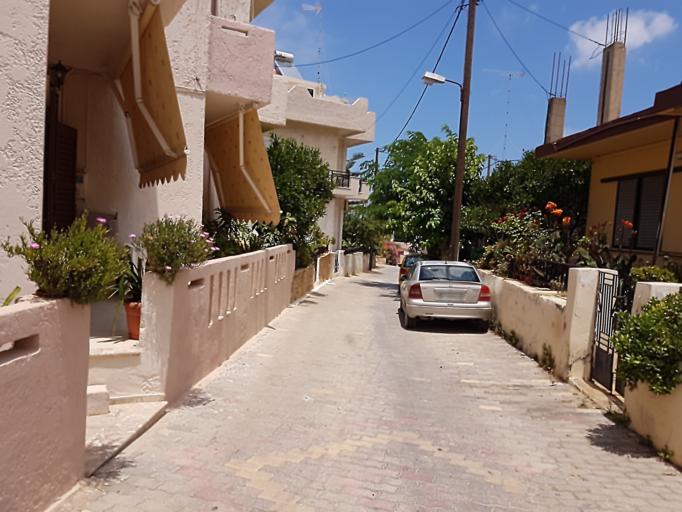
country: GR
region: Crete
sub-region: Nomos Irakleiou
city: Limin Khersonisou
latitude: 35.3075
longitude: 25.3727
